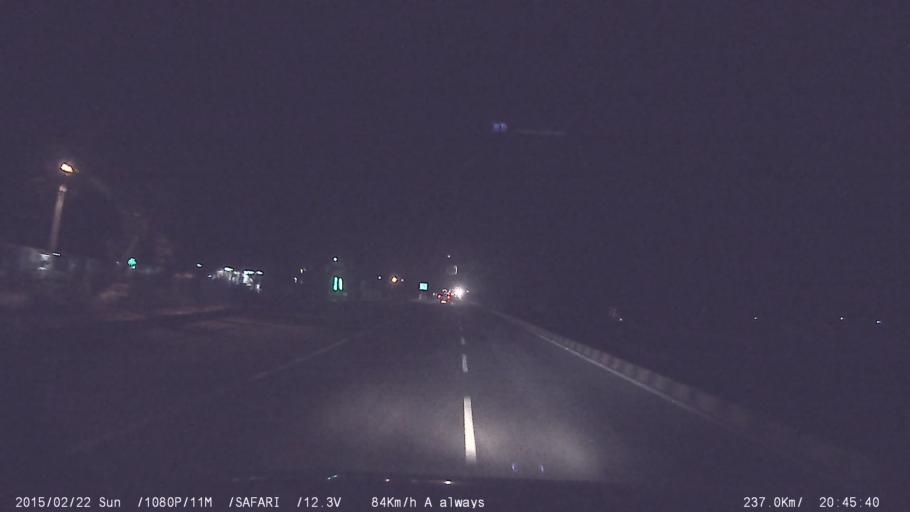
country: IN
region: Tamil Nadu
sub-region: Dindigul
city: Vedasandur
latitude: 10.4720
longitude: 77.9482
